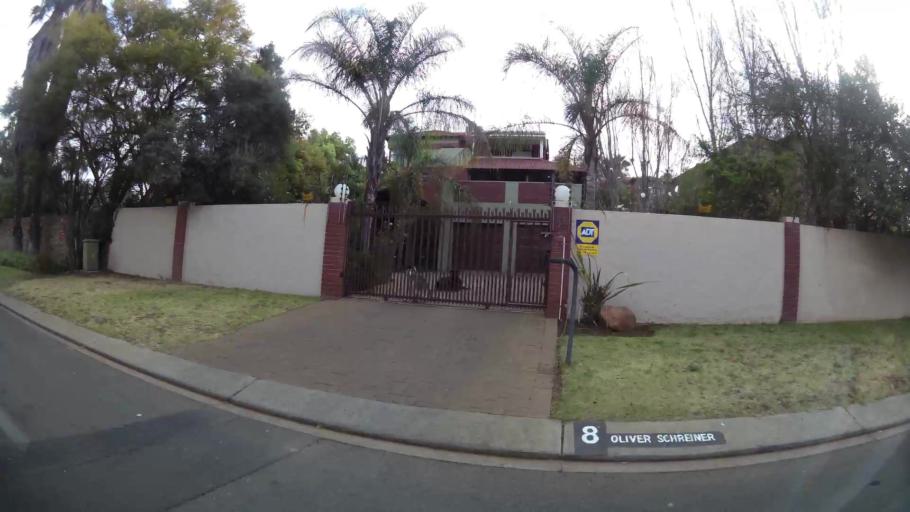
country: ZA
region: Orange Free State
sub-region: Mangaung Metropolitan Municipality
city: Bloemfontein
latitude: -29.0806
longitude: 26.2030
